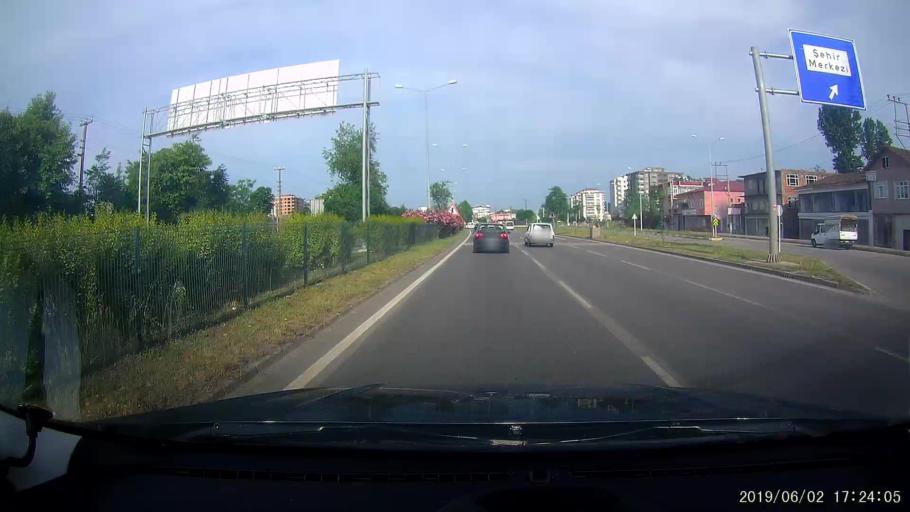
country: TR
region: Samsun
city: Carsamba
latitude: 41.2060
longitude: 36.6965
